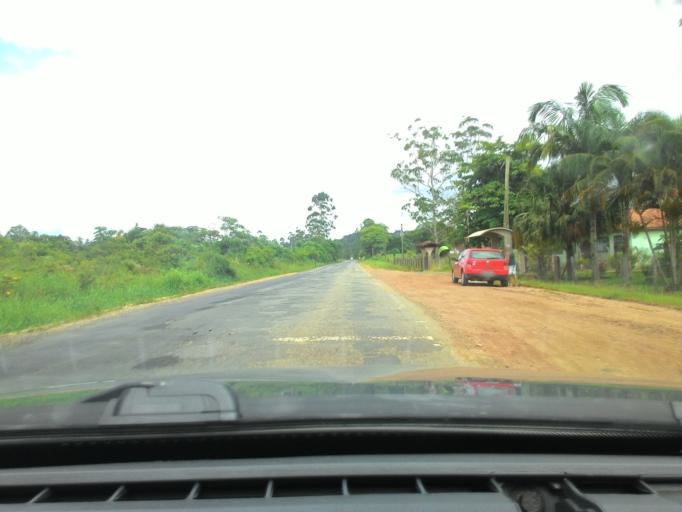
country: BR
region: Sao Paulo
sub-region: Pariquera-Acu
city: Pariquera Acu
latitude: -24.7331
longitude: -47.8228
